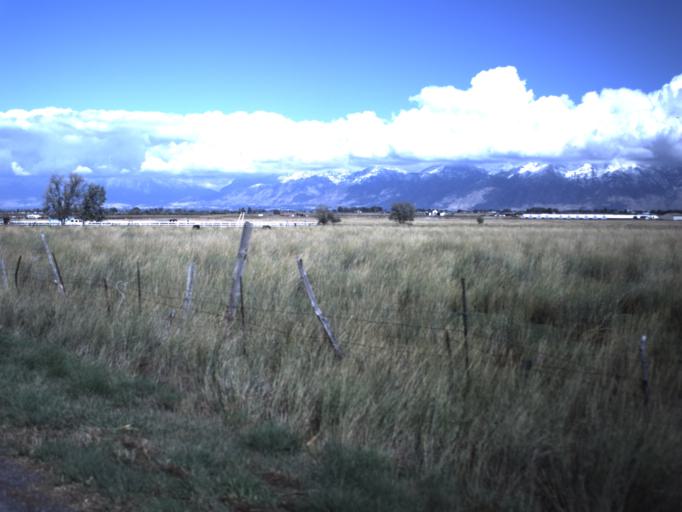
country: US
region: Utah
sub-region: Utah County
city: West Mountain
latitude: 40.0886
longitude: -111.7880
